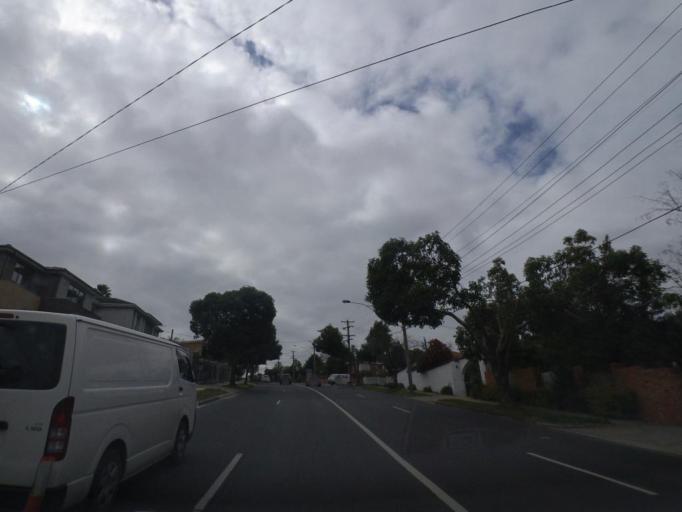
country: AU
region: Victoria
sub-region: Manningham
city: Doncaster
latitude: -37.7946
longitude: 145.1199
